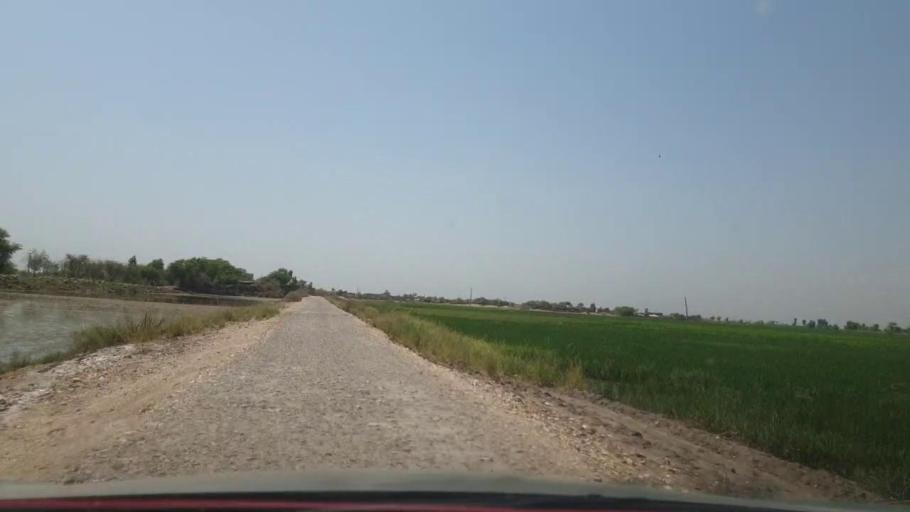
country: PK
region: Sindh
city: Warah
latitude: 27.4859
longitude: 67.7349
